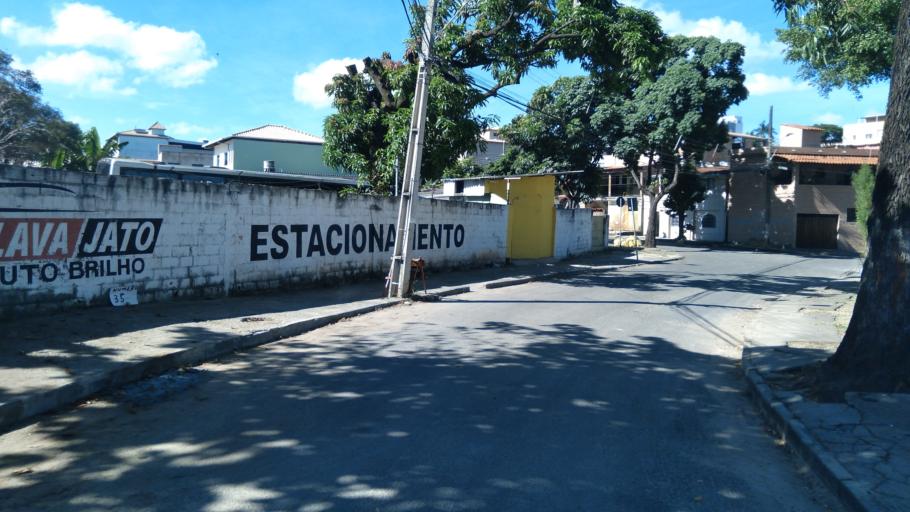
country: BR
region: Minas Gerais
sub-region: Belo Horizonte
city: Belo Horizonte
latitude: -19.8551
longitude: -43.9126
